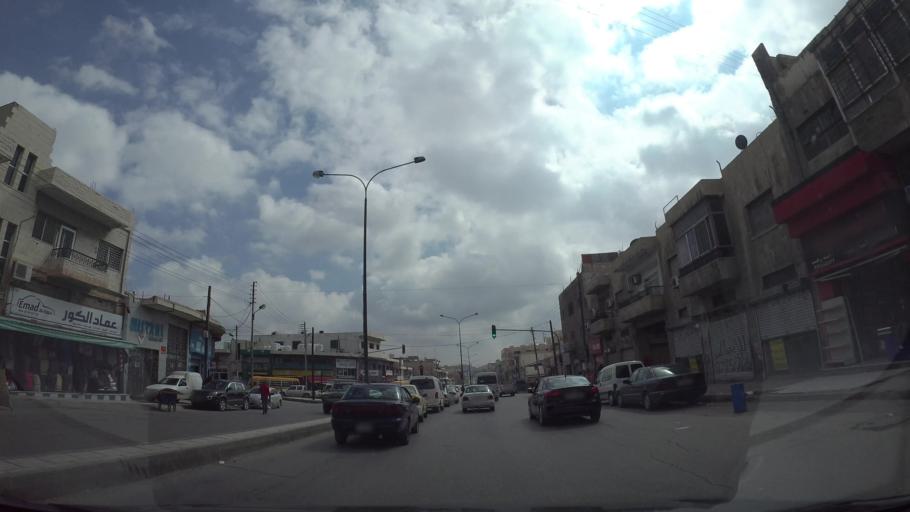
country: JO
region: Amman
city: Al Quwaysimah
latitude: 31.9272
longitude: 35.9377
